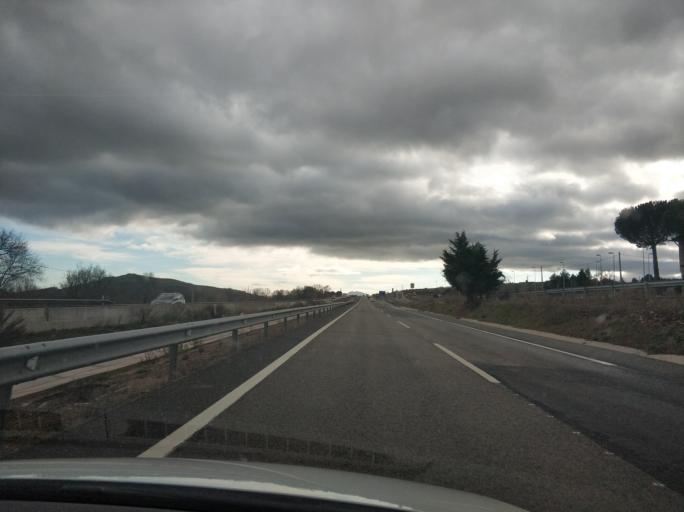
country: ES
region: Madrid
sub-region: Provincia de Madrid
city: Braojos
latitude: 41.0465
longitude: -3.6160
